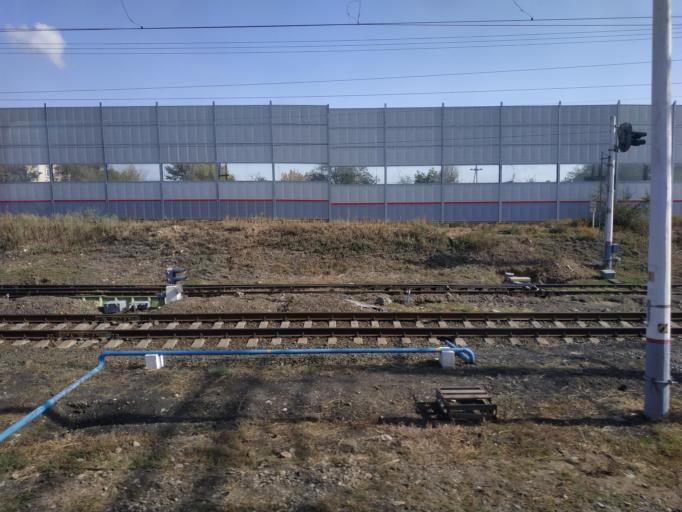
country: RU
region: Volgograd
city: Gumrak
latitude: 48.7754
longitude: 44.3818
